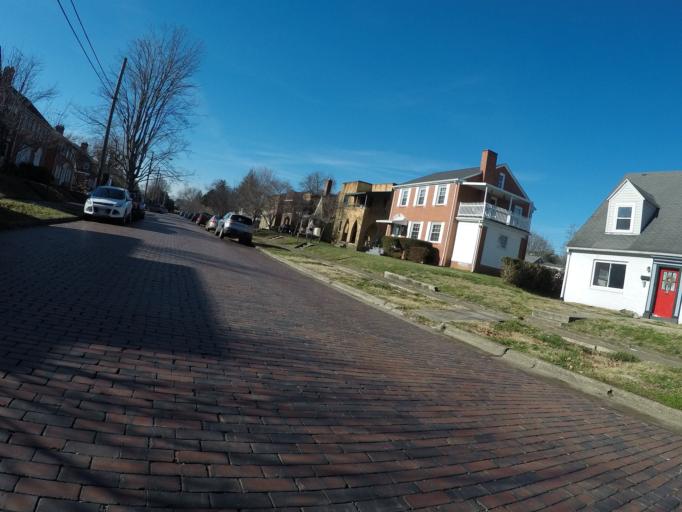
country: US
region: West Virginia
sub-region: Cabell County
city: Huntington
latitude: 38.4107
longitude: -82.4328
